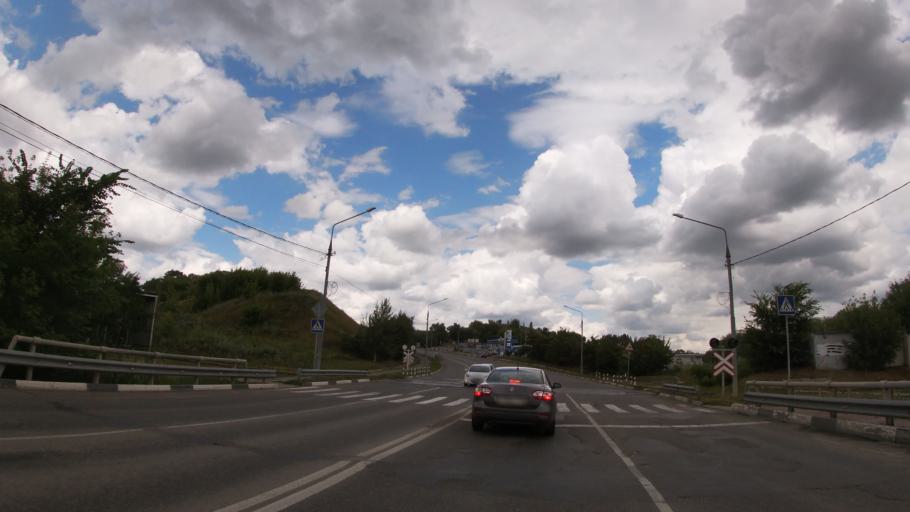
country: RU
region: Belgorod
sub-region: Belgorodskiy Rayon
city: Belgorod
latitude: 50.6086
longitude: 36.6132
